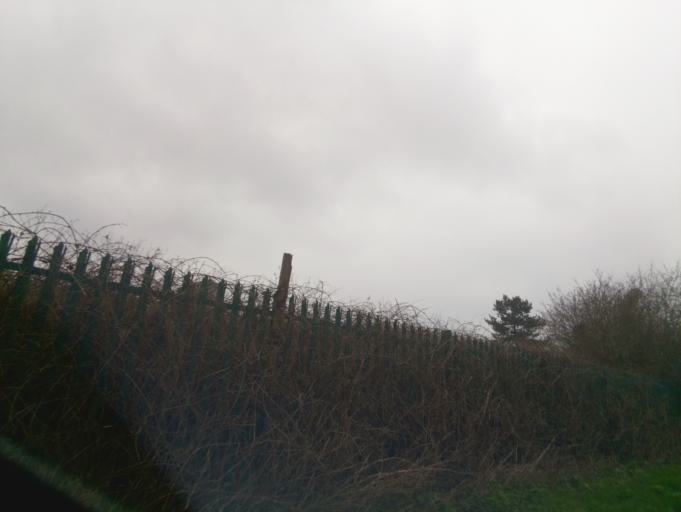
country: GB
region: England
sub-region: South Gloucestershire
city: Charfield
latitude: 51.6255
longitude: -2.3974
